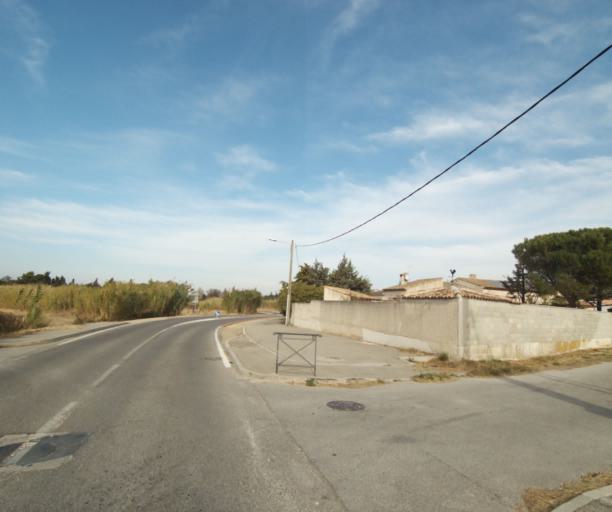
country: FR
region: Provence-Alpes-Cote d'Azur
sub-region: Departement des Bouches-du-Rhone
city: Gignac-la-Nerthe
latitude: 43.3904
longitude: 5.2212
